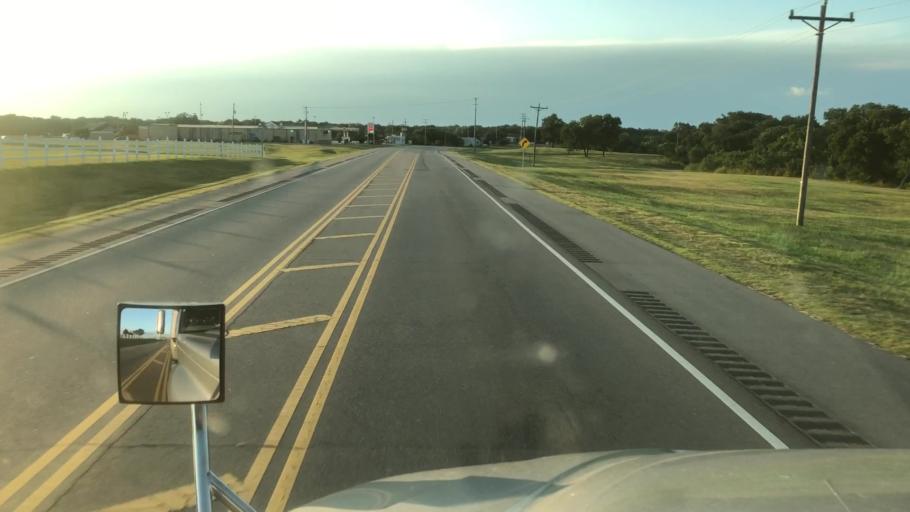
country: US
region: Oklahoma
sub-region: Osage County
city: McCord
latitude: 36.4862
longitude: -97.0711
